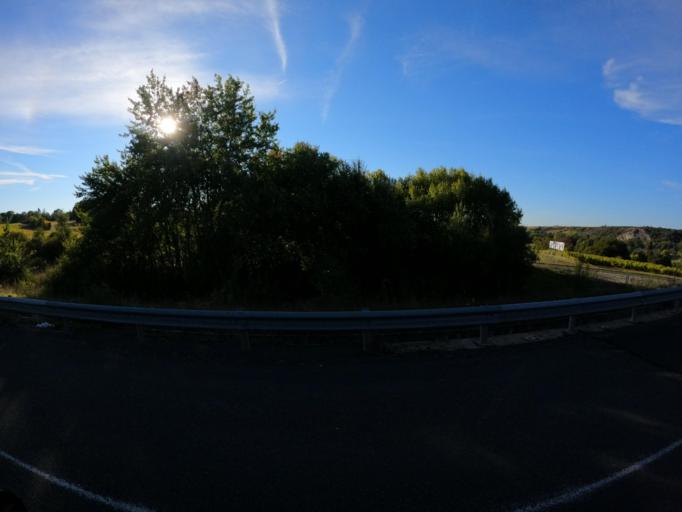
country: FR
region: Pays de la Loire
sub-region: Departement de Maine-et-Loire
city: Beaulieu-sur-Layon
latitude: 47.3089
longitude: -0.6074
